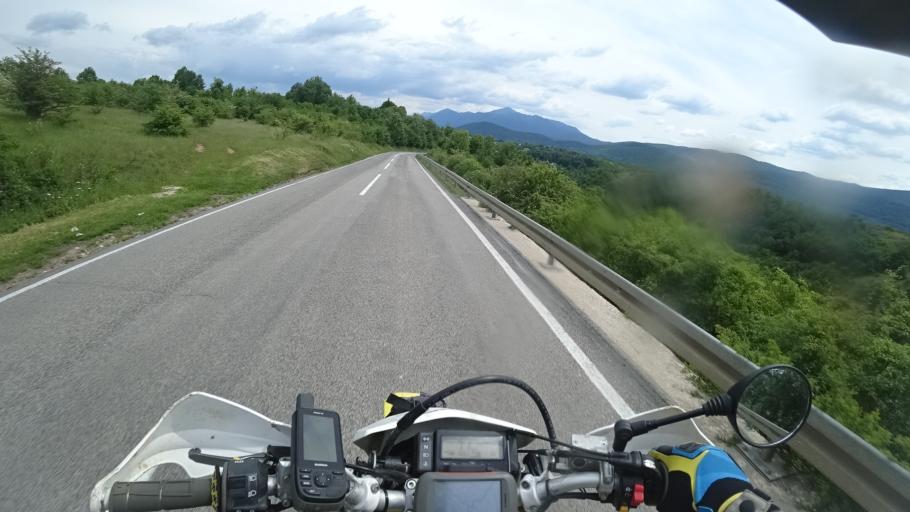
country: BA
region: Federation of Bosnia and Herzegovina
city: Izacic
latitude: 44.9243
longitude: 15.7039
